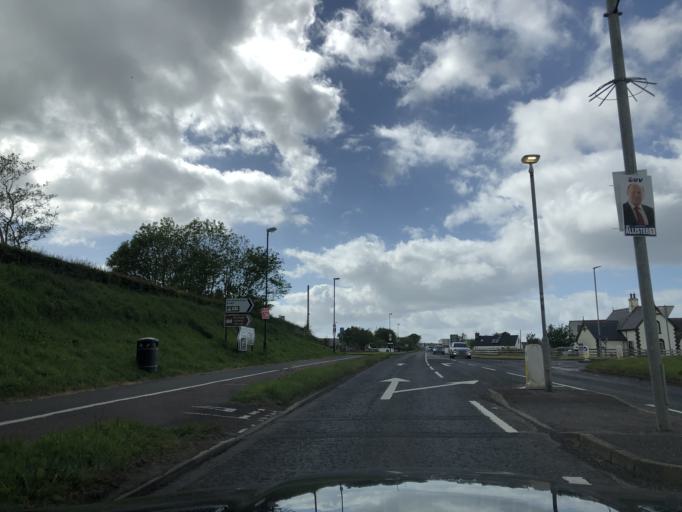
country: GB
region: Northern Ireland
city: Bushmills
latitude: 55.2059
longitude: -6.5284
